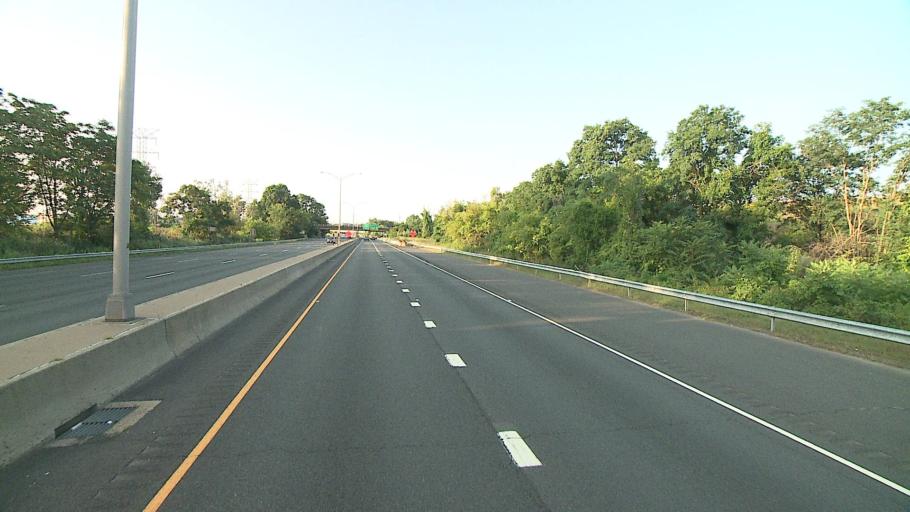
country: US
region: Connecticut
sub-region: Hartford County
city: Wethersfield
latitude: 41.7412
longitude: -72.6619
